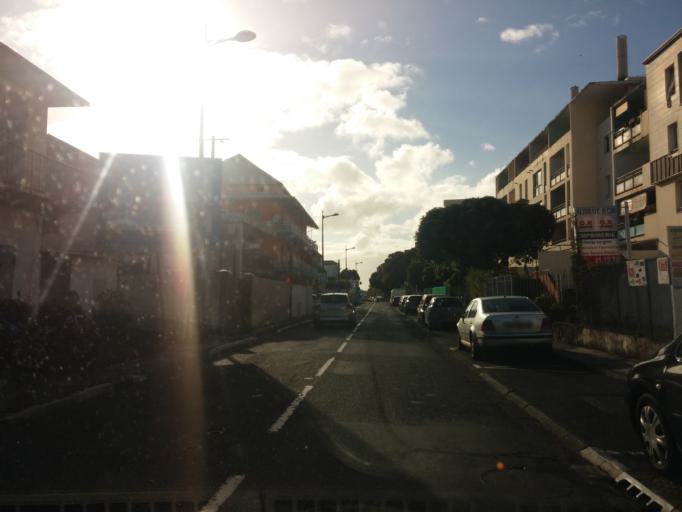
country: RE
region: Reunion
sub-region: Reunion
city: Saint-Denis
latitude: -20.8879
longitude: 55.4536
